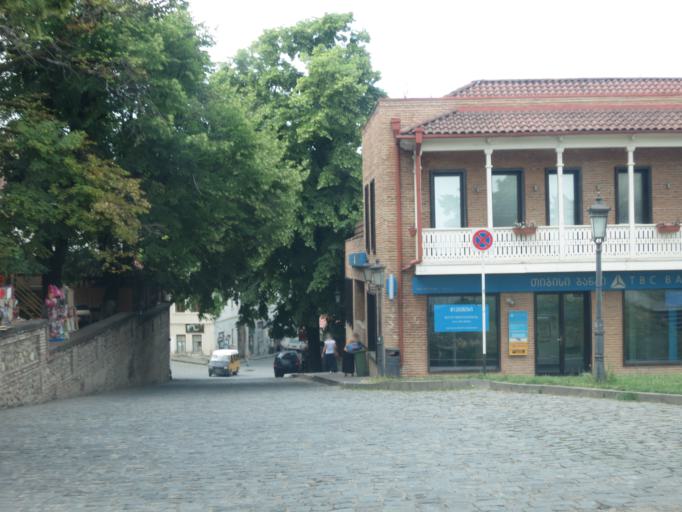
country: GE
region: Kakheti
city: Sighnaghi
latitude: 41.6200
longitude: 45.9225
